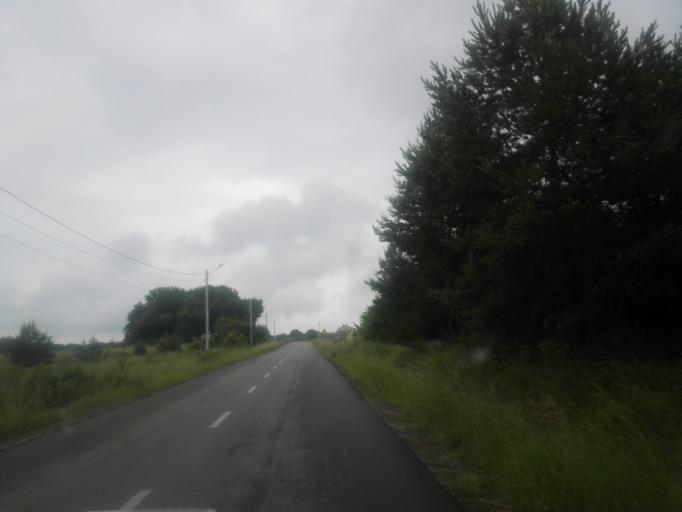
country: PL
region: Silesian Voivodeship
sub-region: Powiat czestochowski
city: Potok Zloty
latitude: 50.7008
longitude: 19.3629
